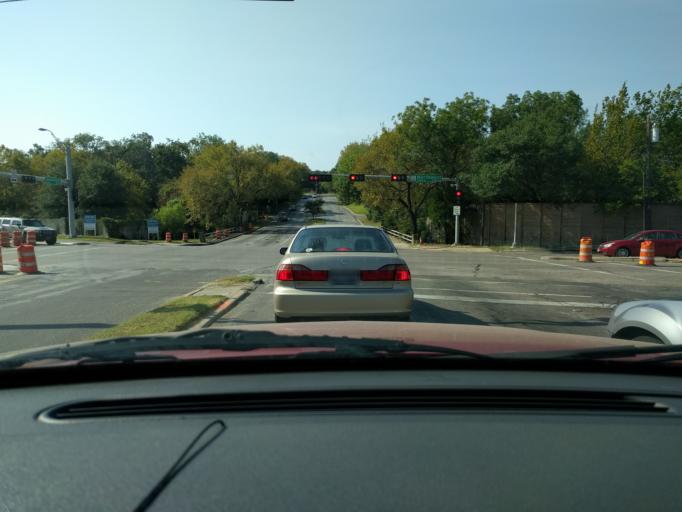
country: US
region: Texas
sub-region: Dallas County
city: University Park
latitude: 32.8668
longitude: -96.8221
